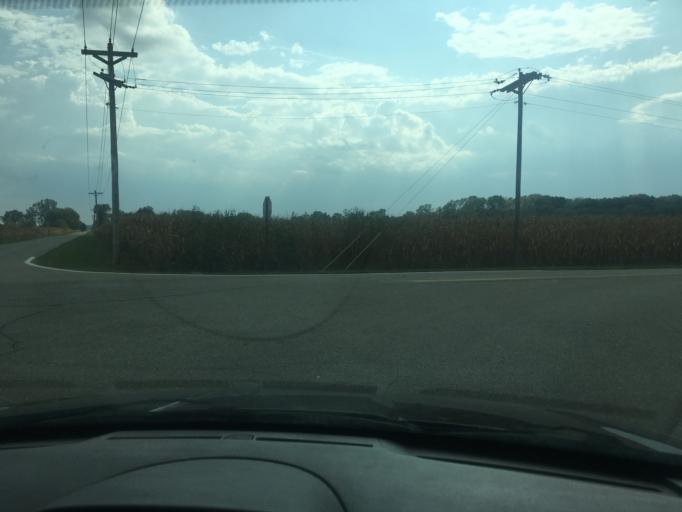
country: US
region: Ohio
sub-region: Champaign County
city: Urbana
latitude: 40.1563
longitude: -83.8141
